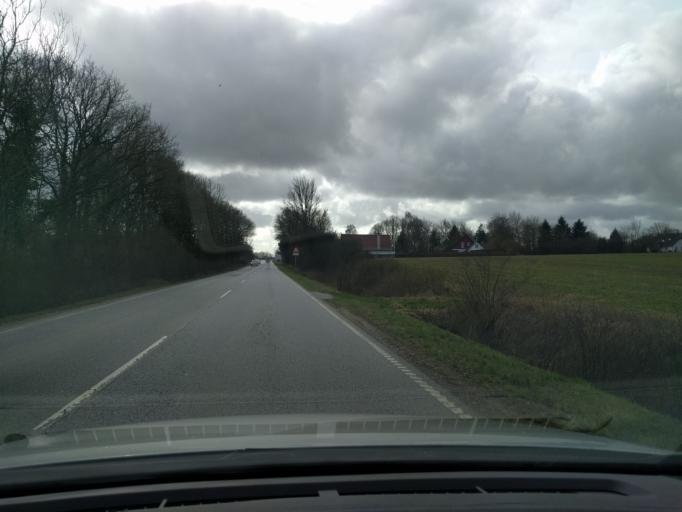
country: DK
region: South Denmark
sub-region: Vejen Kommune
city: Rodding
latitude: 55.3173
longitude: 9.1459
